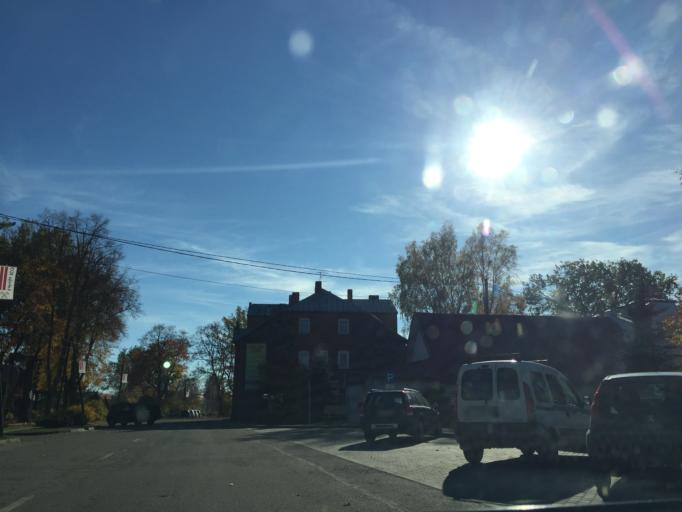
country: LV
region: Incukalns
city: Incukalns
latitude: 57.0981
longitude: 24.6865
